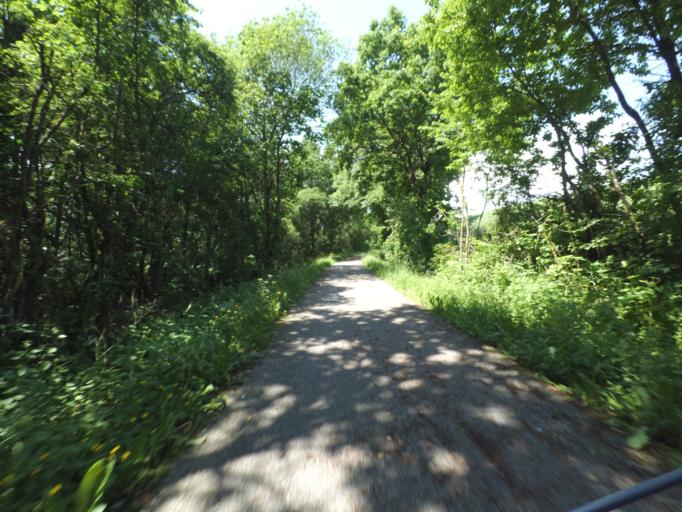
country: DE
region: Rheinland-Pfalz
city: Emmelshausen
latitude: 50.1431
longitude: 7.5661
